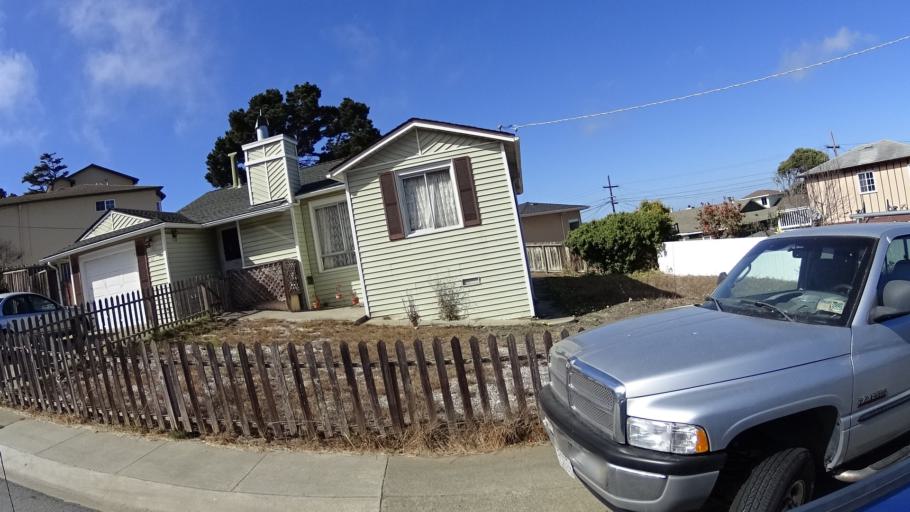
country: US
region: California
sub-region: San Mateo County
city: Broadmoor
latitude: 37.6910
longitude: -122.4811
